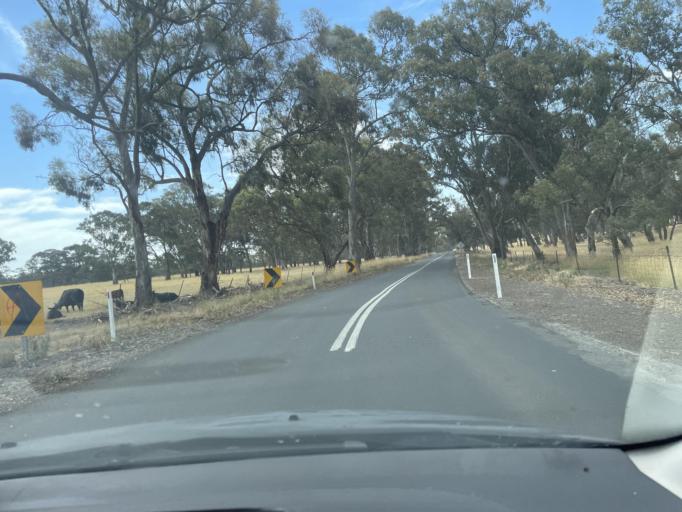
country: AU
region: South Australia
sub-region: Clare and Gilbert Valleys
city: Clare
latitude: -33.8998
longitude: 138.6419
